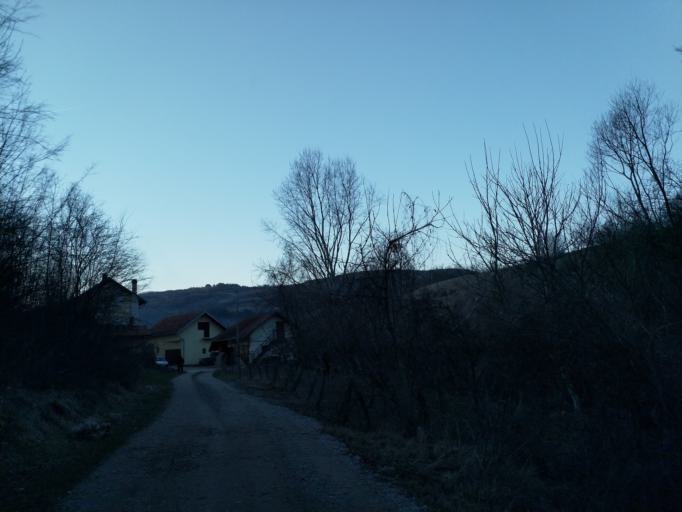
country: RS
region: Central Serbia
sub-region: Pomoravski Okrug
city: Paracin
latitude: 43.9292
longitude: 21.5224
